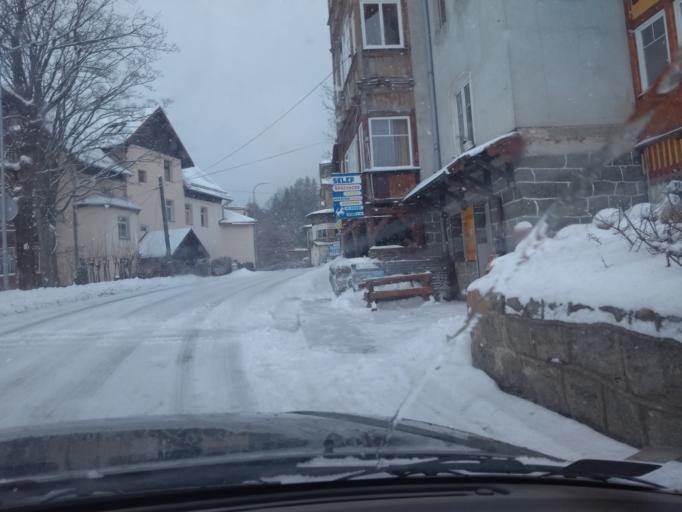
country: PL
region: Lower Silesian Voivodeship
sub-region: Powiat jeleniogorski
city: Karpacz
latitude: 50.7809
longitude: 15.7246
